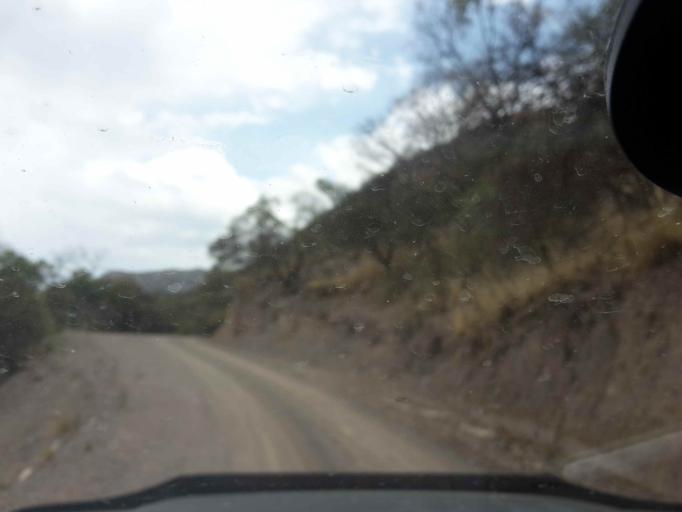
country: BO
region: Cochabamba
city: Sipe Sipe
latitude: -17.5226
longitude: -66.5563
